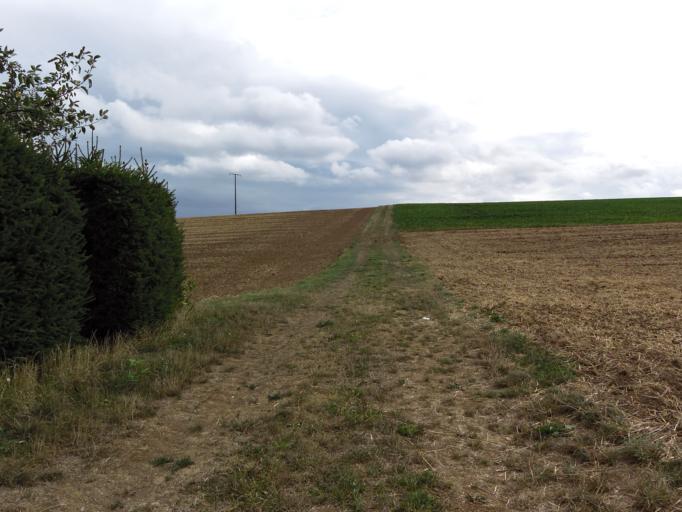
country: DE
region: Bavaria
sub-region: Regierungsbezirk Unterfranken
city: Rimpar
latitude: 49.8569
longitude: 9.9441
